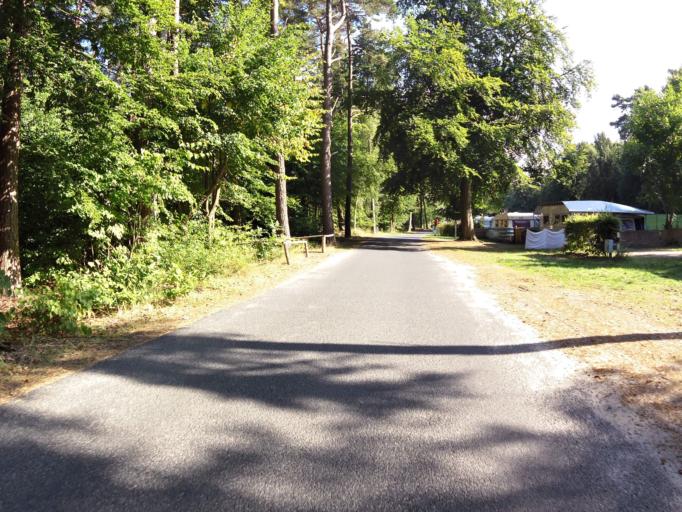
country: DE
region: Mecklenburg-Vorpommern
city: Seebad Bansin
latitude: 53.9980
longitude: 14.1029
